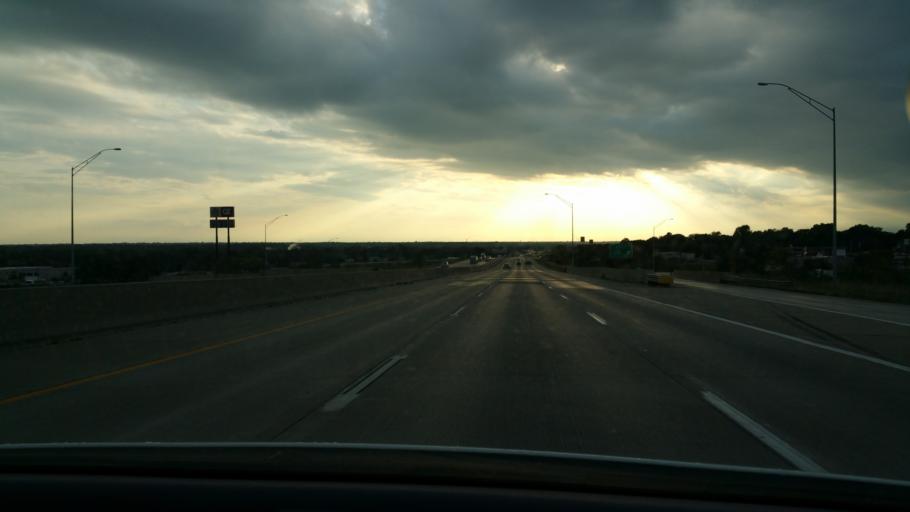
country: US
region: Iowa
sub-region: Polk County
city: Saylorville
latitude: 41.6502
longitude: -93.5939
